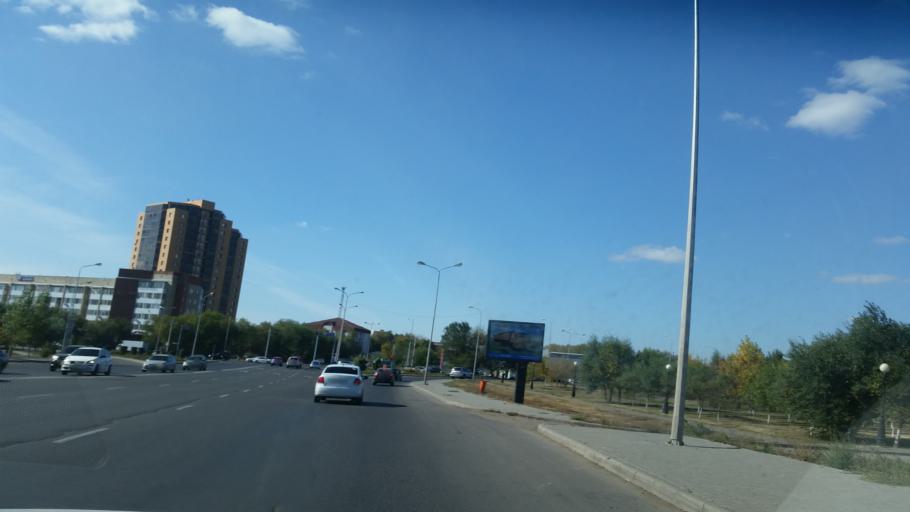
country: KZ
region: Astana Qalasy
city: Astana
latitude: 51.1647
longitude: 71.4774
